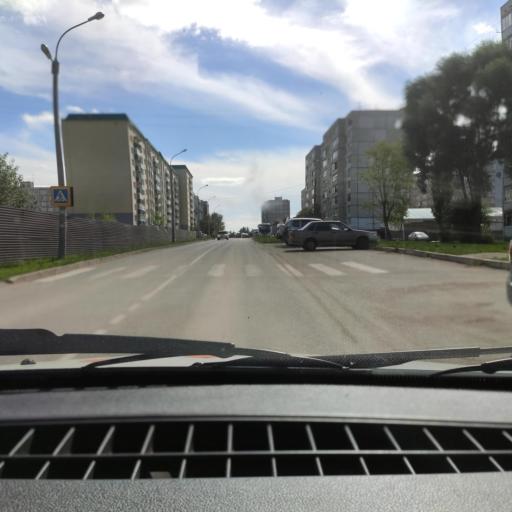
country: RU
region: Bashkortostan
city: Blagoveshchensk
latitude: 55.0522
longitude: 55.9620
